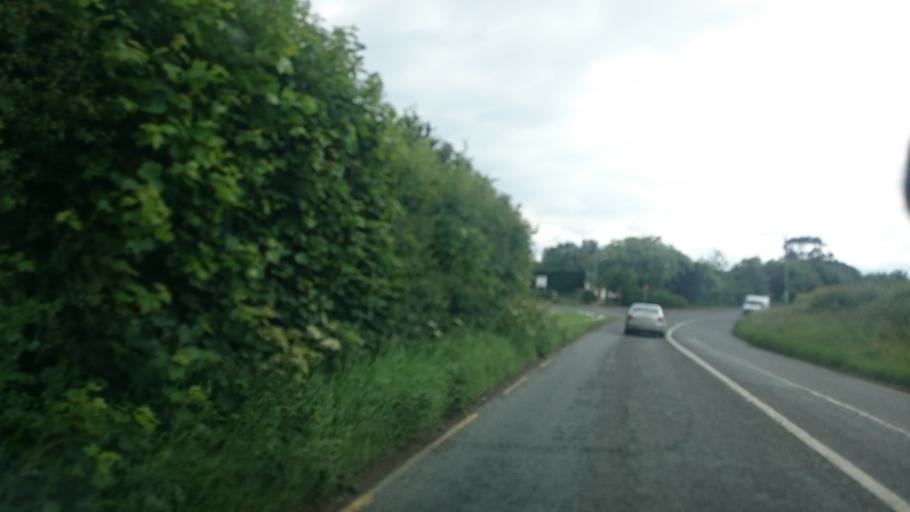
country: IE
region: Leinster
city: Lusk
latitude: 53.5058
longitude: -6.1866
